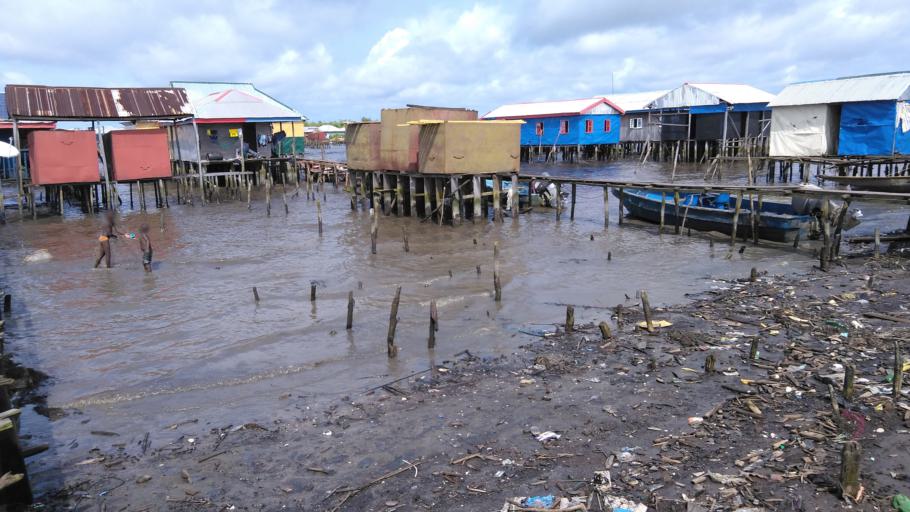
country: NG
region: Ondo
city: Igbekebo
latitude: 5.9230
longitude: 4.9656
